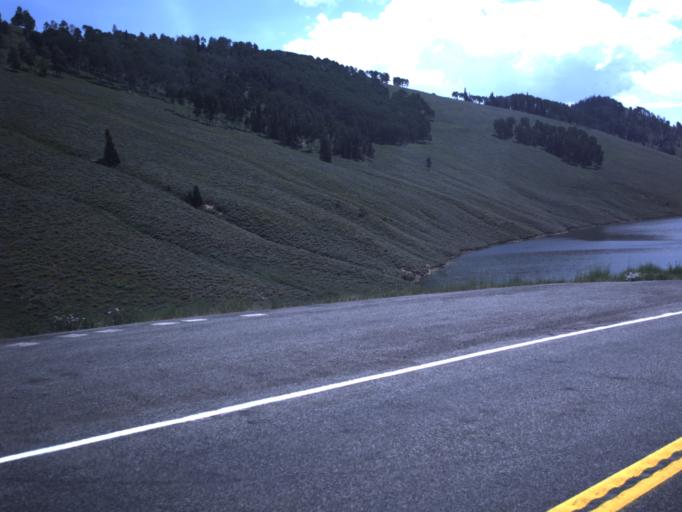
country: US
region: Utah
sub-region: Sanpete County
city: Fairview
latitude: 39.6453
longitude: -111.2384
